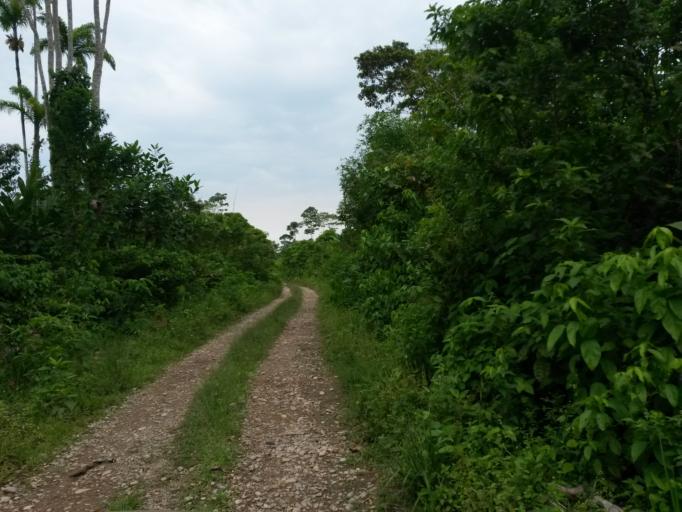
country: CO
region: Putumayo
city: Puerto Guzman
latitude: 1.0188
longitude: -76.3667
